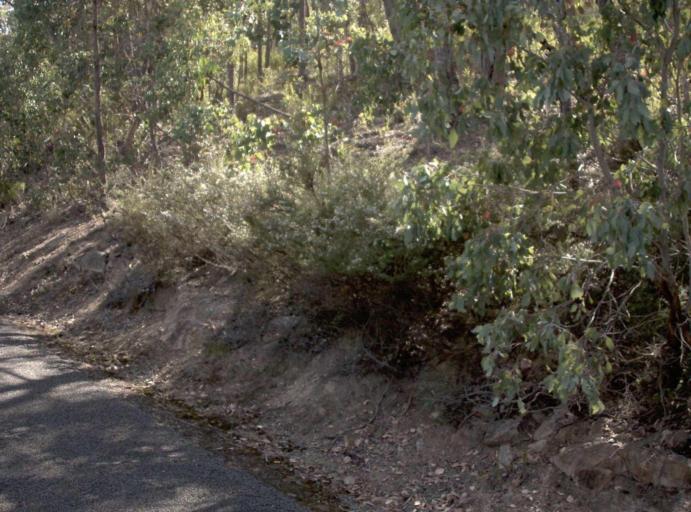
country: AU
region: Victoria
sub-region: East Gippsland
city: Lakes Entrance
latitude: -37.4790
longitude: 148.1241
